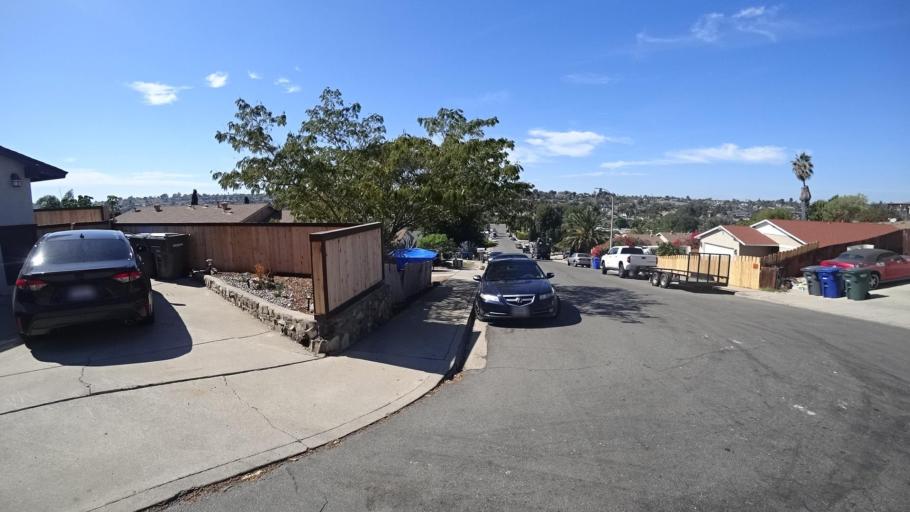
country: US
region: California
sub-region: San Diego County
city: La Presa
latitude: 32.7182
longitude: -117.0107
